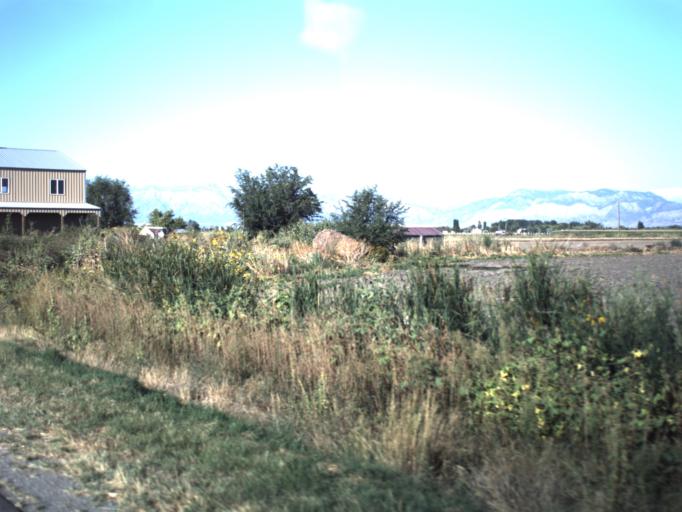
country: US
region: Utah
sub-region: Weber County
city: Hooper
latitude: 41.1477
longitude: -112.1229
